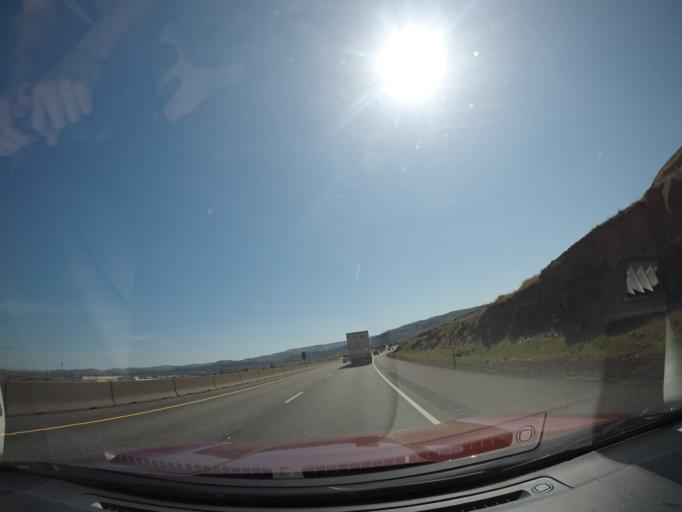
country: US
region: Oregon
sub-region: Wasco County
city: Chenoweth
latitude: 45.6400
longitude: -121.2092
